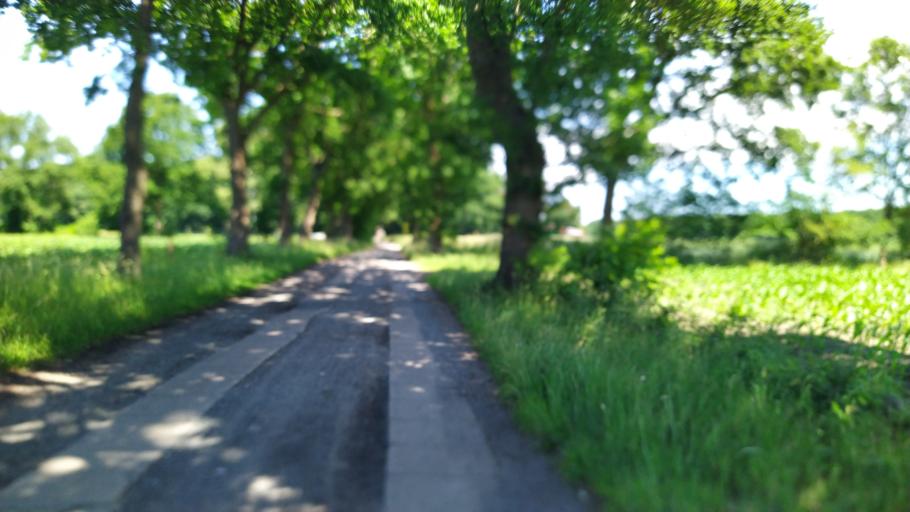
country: DE
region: Lower Saxony
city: Bargstedt
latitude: 53.4914
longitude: 9.4361
